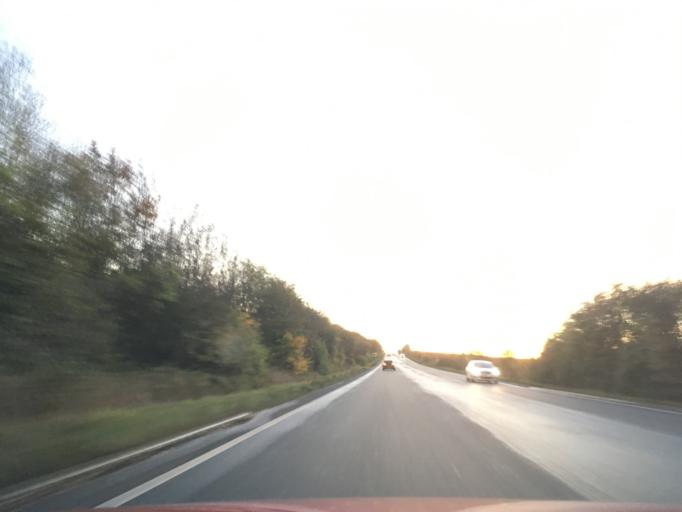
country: GB
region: England
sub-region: Worcestershire
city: Evesham
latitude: 52.0500
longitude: -1.9680
